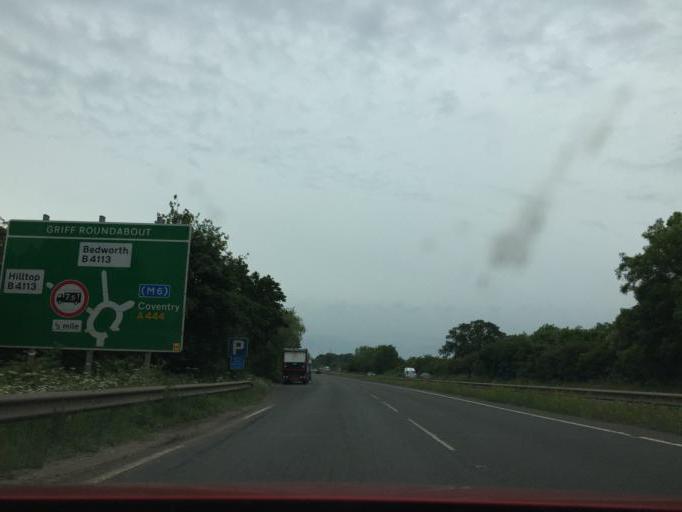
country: GB
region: England
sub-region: Warwickshire
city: Attleborough
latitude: 52.5024
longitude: -1.4756
